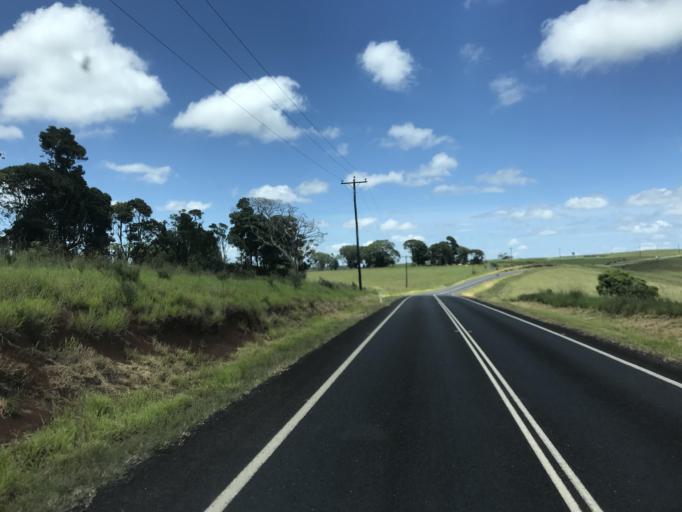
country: AU
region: Queensland
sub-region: Tablelands
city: Ravenshoe
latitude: -17.4935
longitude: 145.4751
